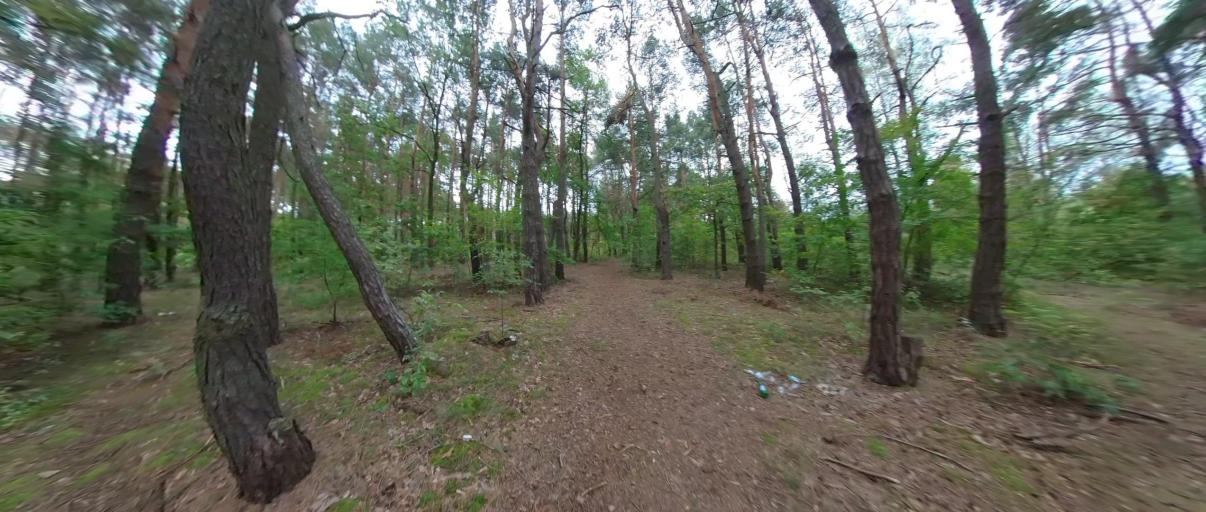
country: PL
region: Masovian Voivodeship
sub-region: Powiat bialobrzeski
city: Bialobrzegi
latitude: 51.6473
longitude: 20.9641
